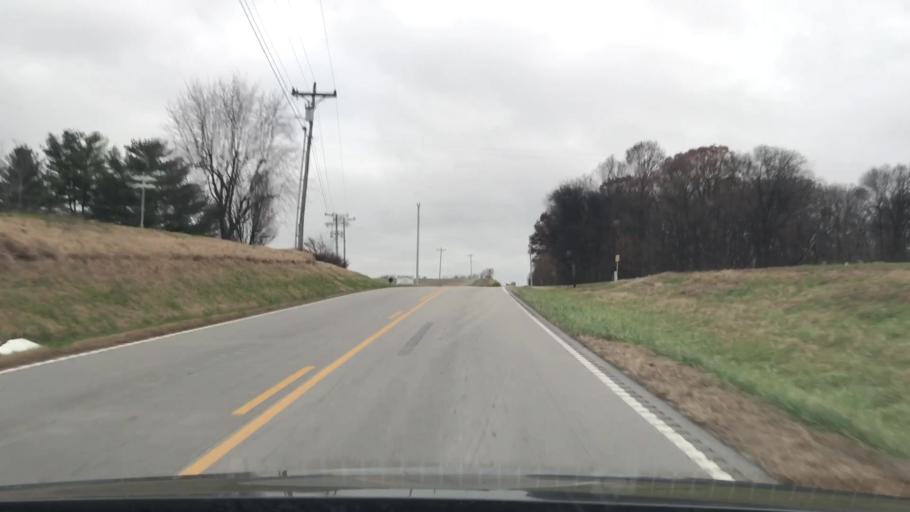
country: US
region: Kentucky
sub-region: Todd County
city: Guthrie
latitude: 36.6848
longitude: -87.2009
